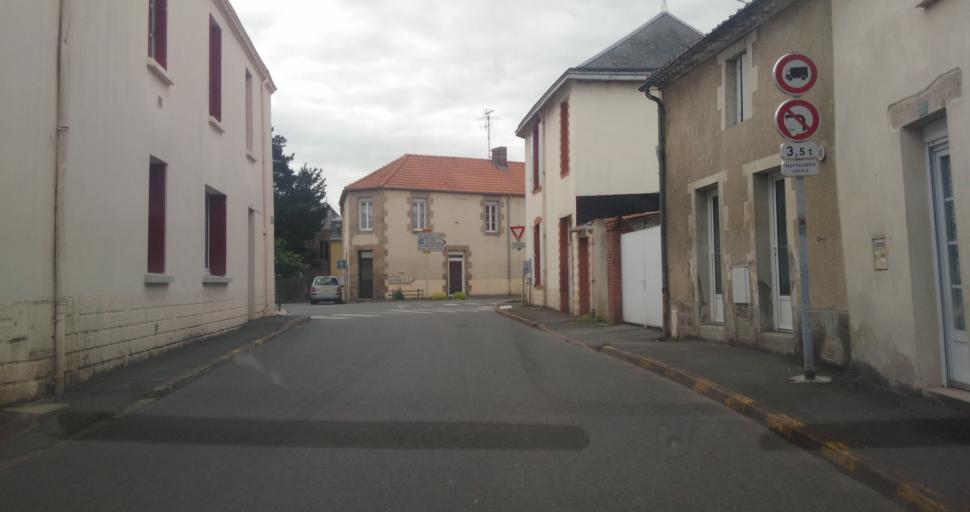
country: FR
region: Pays de la Loire
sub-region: Departement de la Vendee
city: La Chaize-le-Vicomte
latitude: 46.6732
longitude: -1.2953
